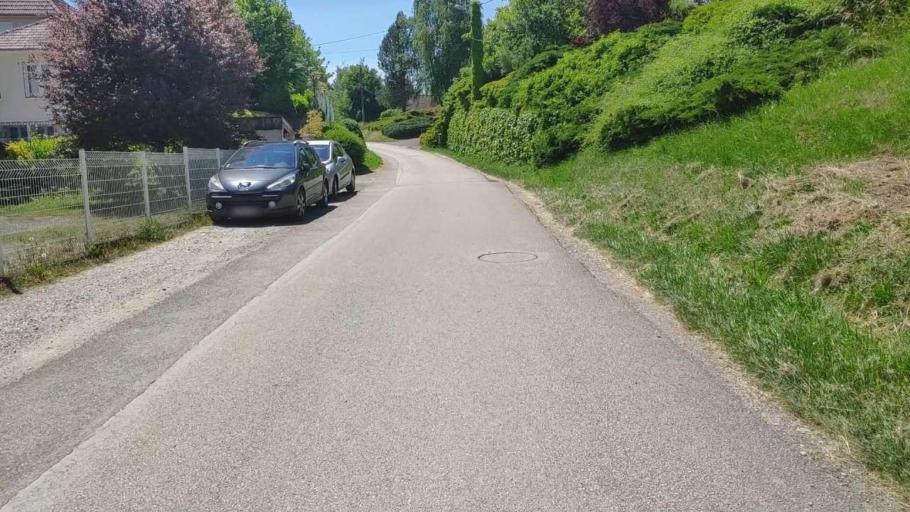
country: FR
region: Franche-Comte
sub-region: Departement du Jura
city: Bletterans
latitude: 46.7450
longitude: 5.4409
